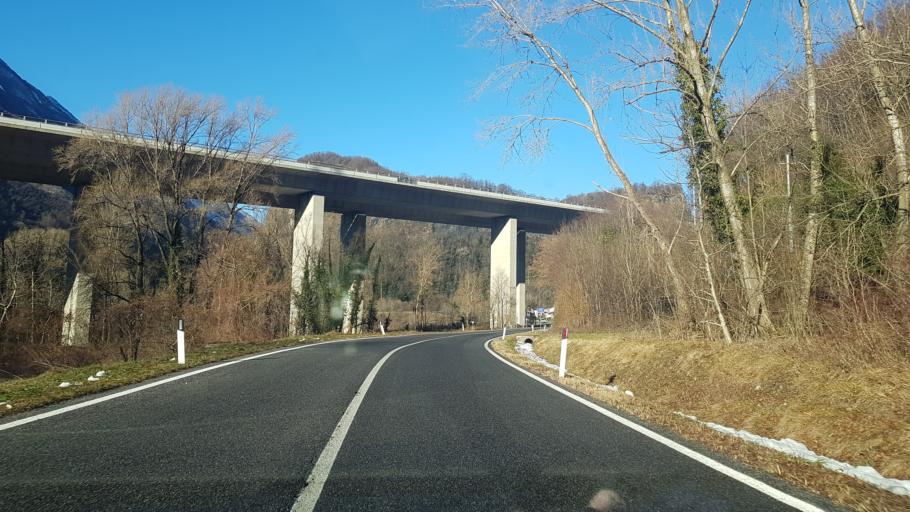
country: IT
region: Friuli Venezia Giulia
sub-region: Provincia di Udine
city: Amaro
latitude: 46.3448
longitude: 13.0729
